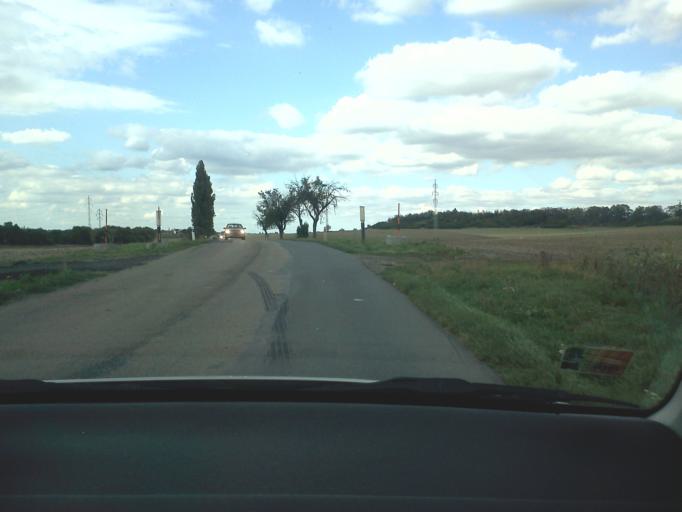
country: CZ
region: Central Bohemia
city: Cesky Brod
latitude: 50.1187
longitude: 14.8584
